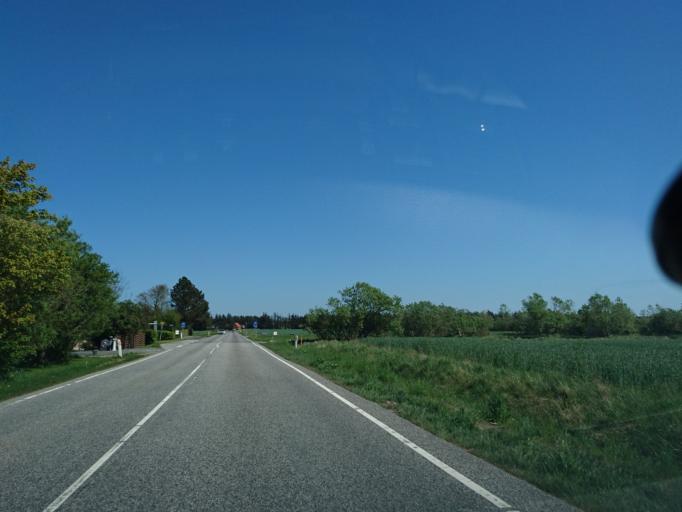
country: DK
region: North Denmark
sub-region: Hjorring Kommune
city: Sindal
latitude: 57.5776
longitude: 10.1673
